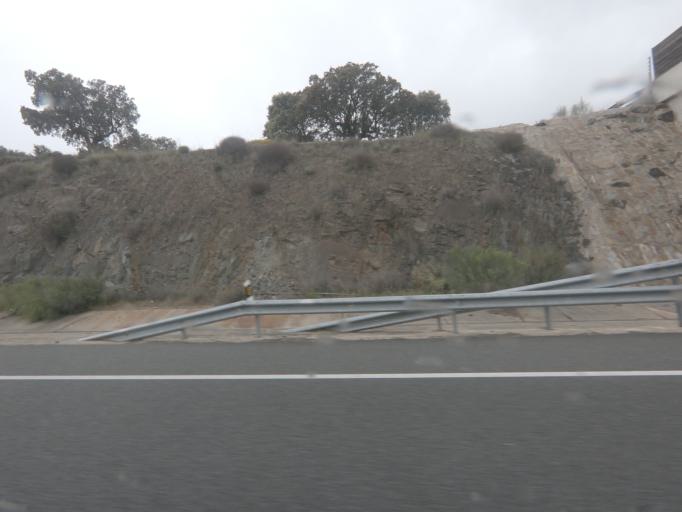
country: ES
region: Extremadura
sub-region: Provincia de Caceres
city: Plasencia
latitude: 40.0291
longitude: -6.1210
